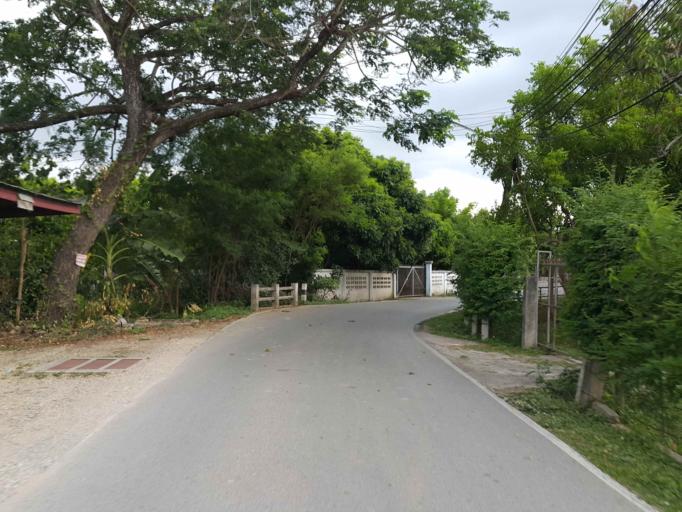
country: TH
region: Chiang Mai
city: Saraphi
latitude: 18.7037
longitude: 99.0286
